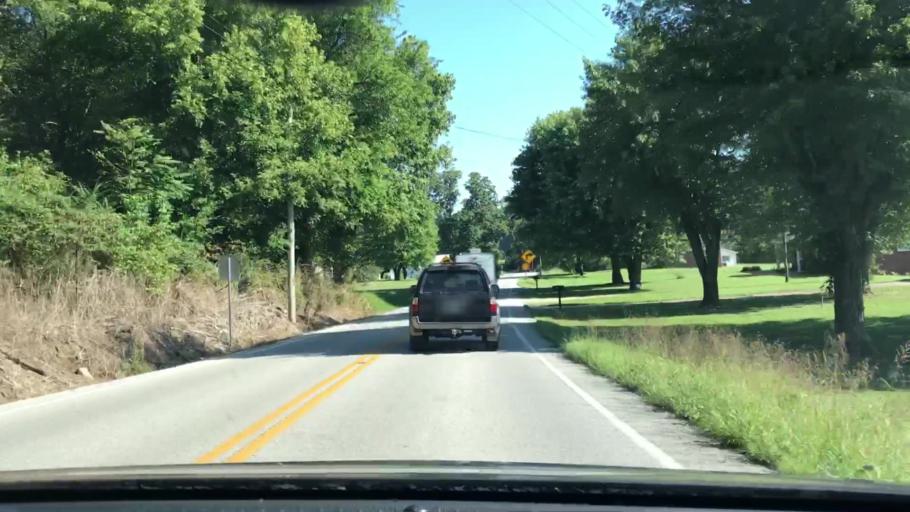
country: US
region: Tennessee
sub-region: Smith County
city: Carthage
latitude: 36.3504
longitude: -85.8957
